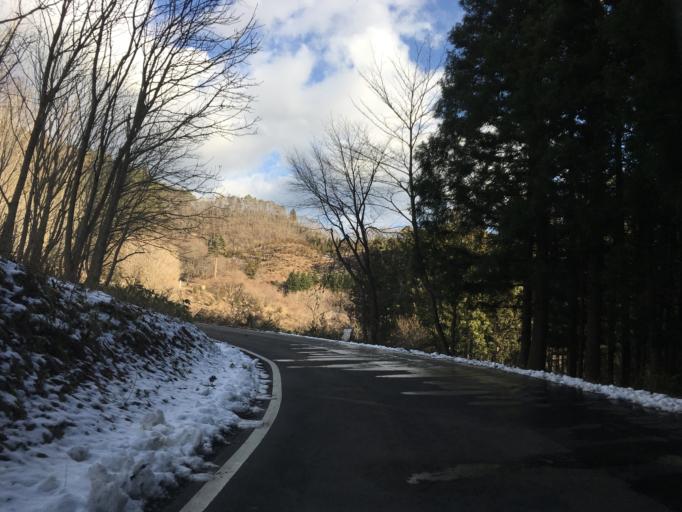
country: JP
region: Miyagi
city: Furukawa
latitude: 38.8115
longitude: 140.8268
